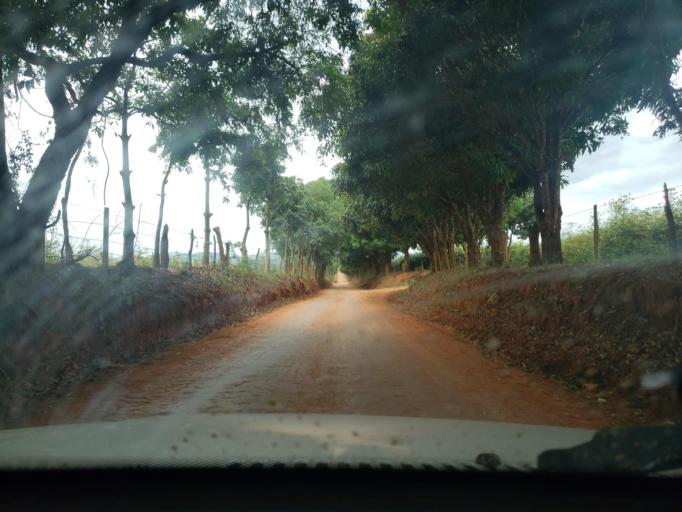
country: BR
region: Minas Gerais
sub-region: Boa Esperanca
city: Boa Esperanca
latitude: -20.9892
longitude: -45.5959
